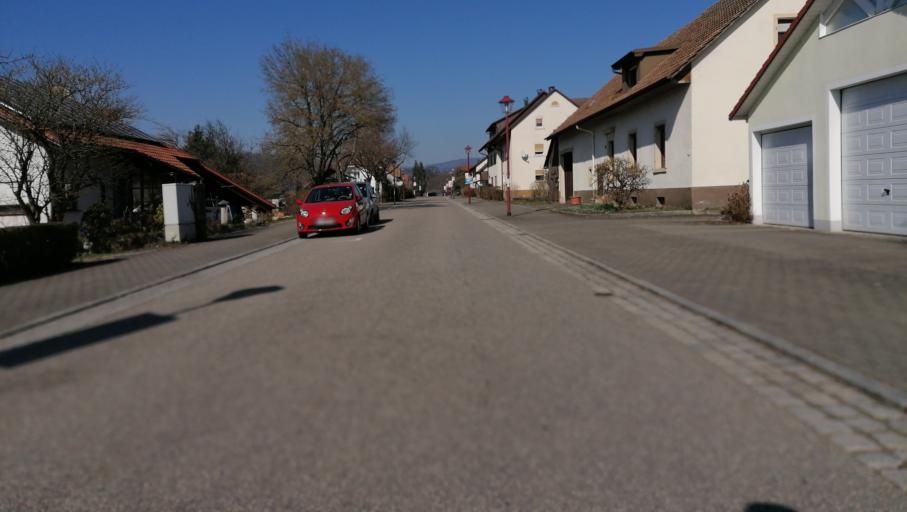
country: CH
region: Aargau
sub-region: Bezirk Rheinfelden
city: Mumpf
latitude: 47.5711
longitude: 7.9130
